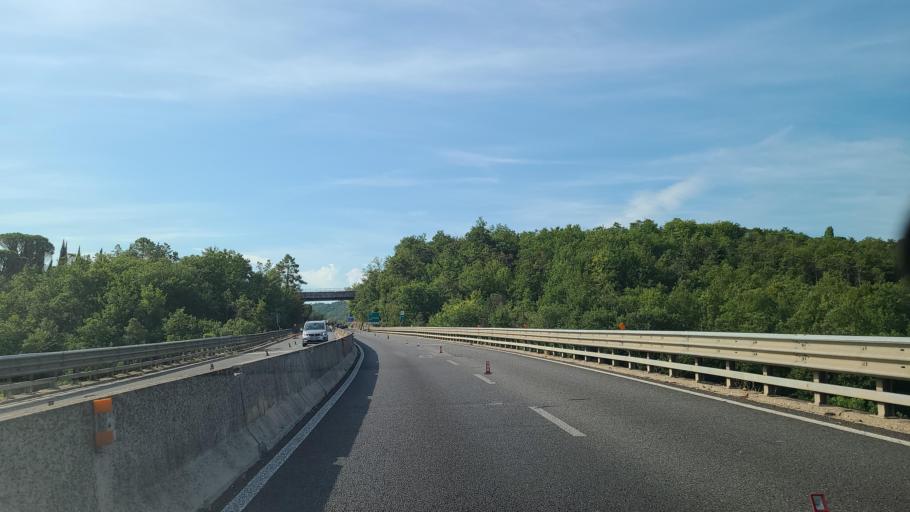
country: IT
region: Tuscany
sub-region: Province of Florence
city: San Casciano in Val di Pesa
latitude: 43.6764
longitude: 11.2103
